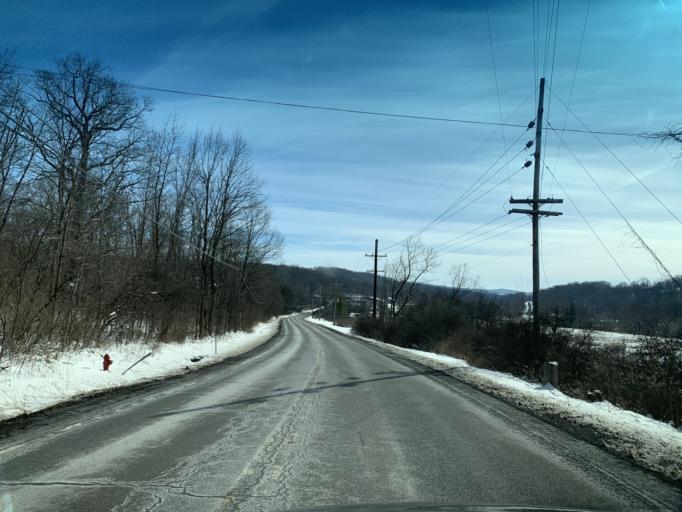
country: US
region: Maryland
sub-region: Allegany County
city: Frostburg
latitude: 39.6209
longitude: -78.9382
